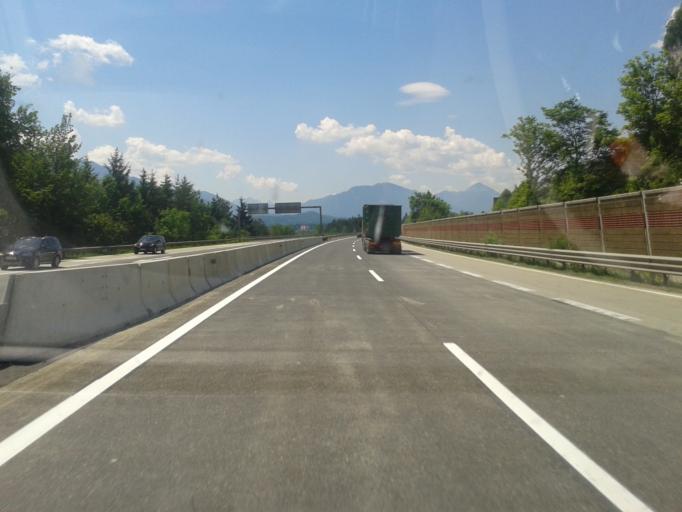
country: AT
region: Carinthia
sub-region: Politischer Bezirk Villach Land
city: Finkenstein am Faaker See
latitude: 46.5703
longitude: 13.8177
